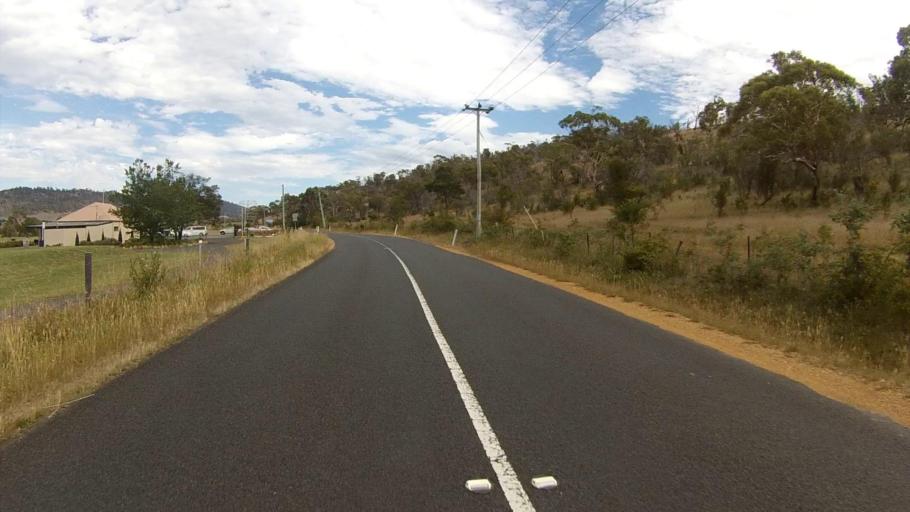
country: AU
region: Tasmania
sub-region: Clarence
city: Cambridge
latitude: -42.7385
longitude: 147.4184
